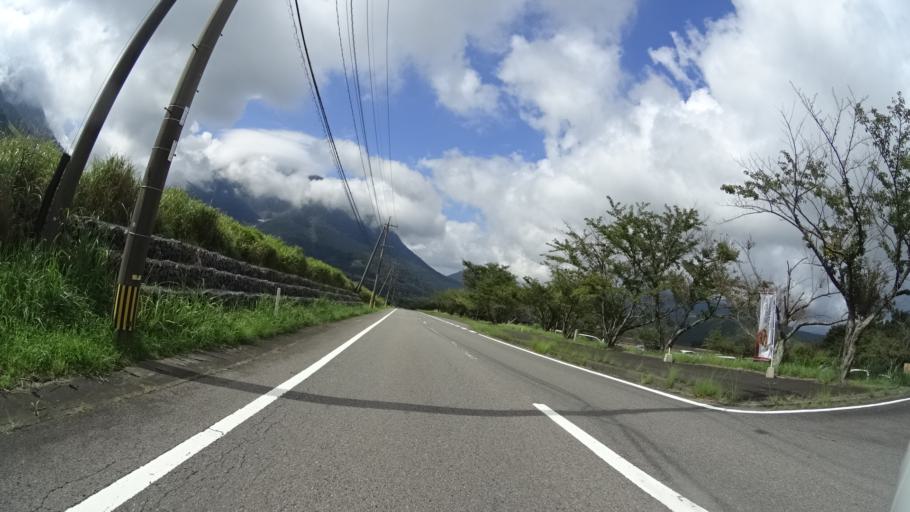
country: JP
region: Oita
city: Beppu
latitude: 33.3142
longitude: 131.4113
